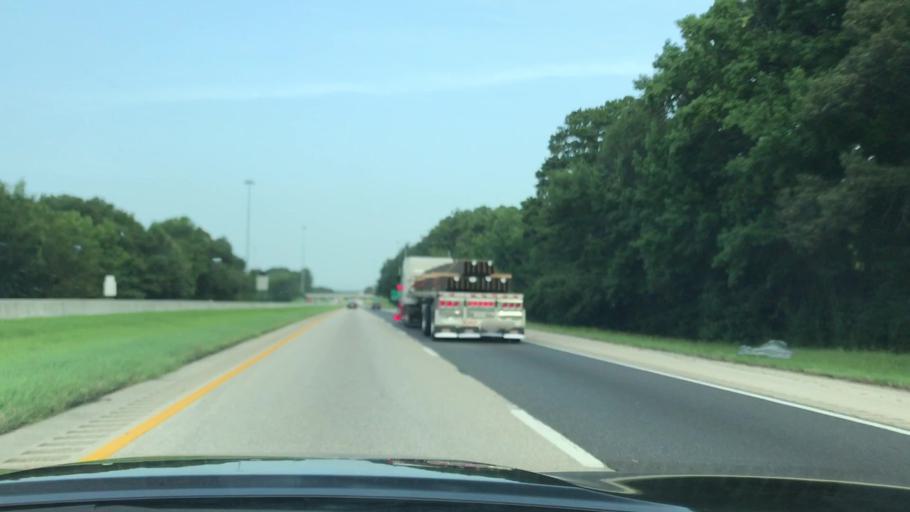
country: US
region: Texas
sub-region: Gregg County
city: Kilgore
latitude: 32.4332
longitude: -94.8549
